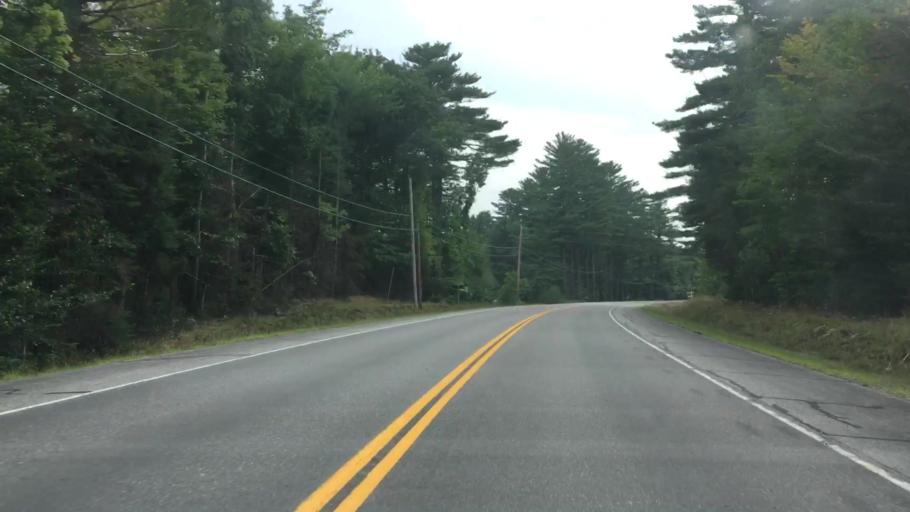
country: US
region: Maine
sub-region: Oxford County
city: Bethel
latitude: 44.4911
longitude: -70.6971
